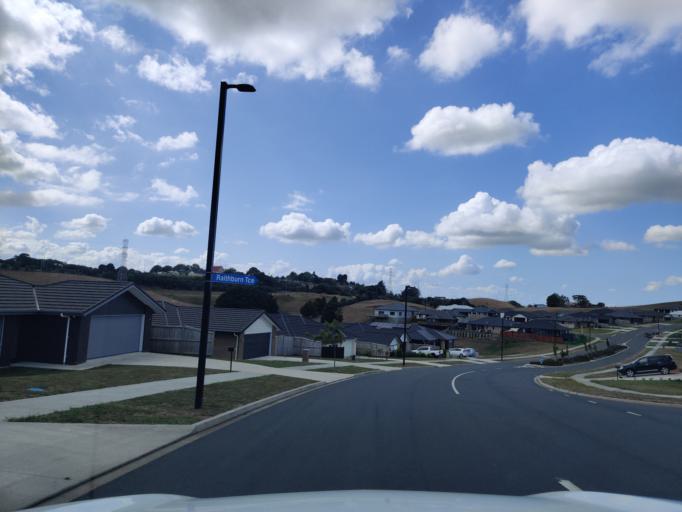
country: NZ
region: Auckland
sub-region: Auckland
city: Pukekohe East
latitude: -37.2354
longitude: 175.0161
